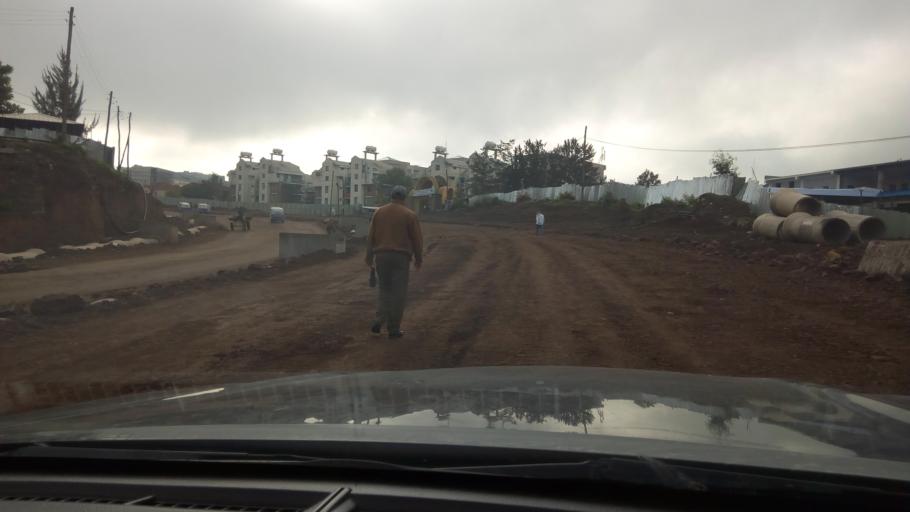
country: ET
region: Amhara
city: Gondar
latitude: 12.5856
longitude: 37.4357
